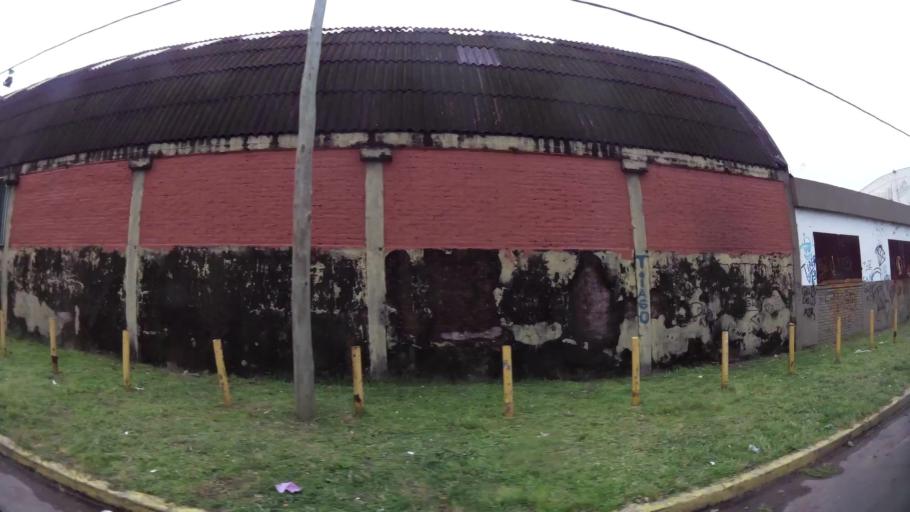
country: AR
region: Buenos Aires
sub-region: Partido de Lanus
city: Lanus
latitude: -34.7121
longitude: -58.3584
